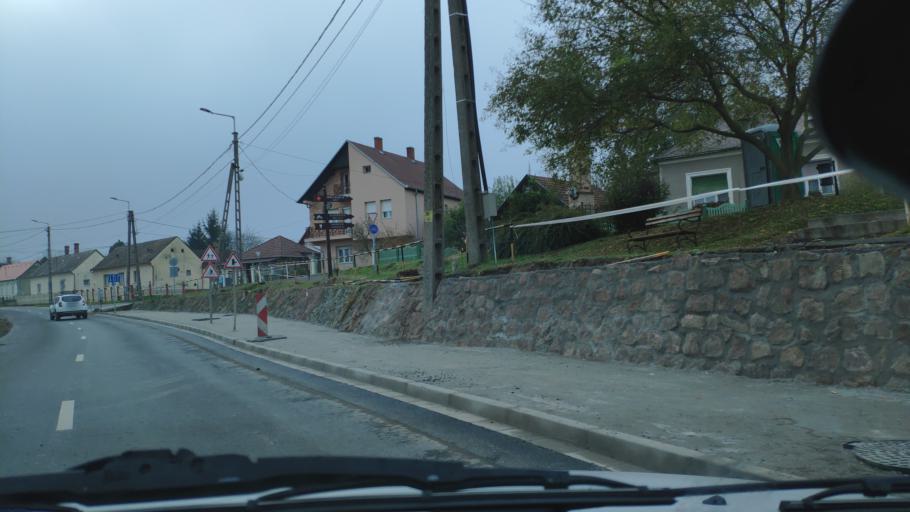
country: HU
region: Zala
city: Zalakomar
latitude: 46.5607
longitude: 17.1230
